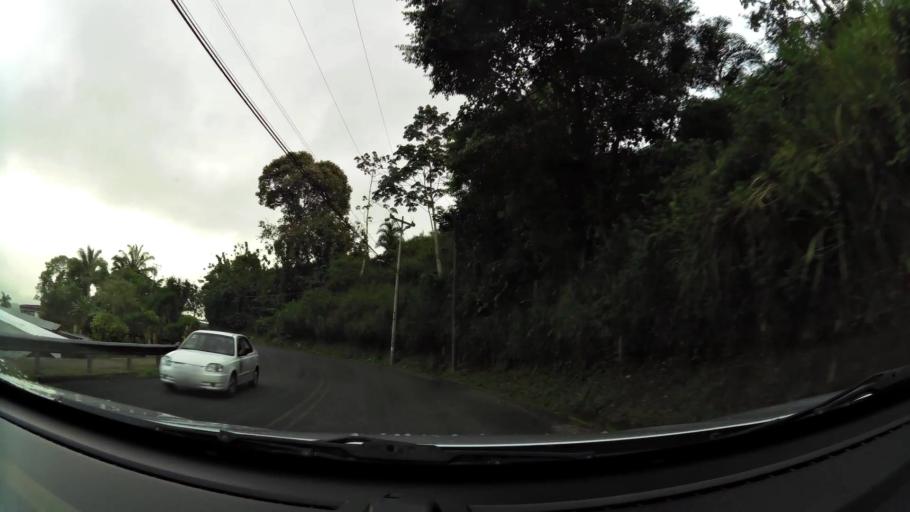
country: CR
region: Cartago
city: Turrialba
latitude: 9.9035
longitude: -83.6880
